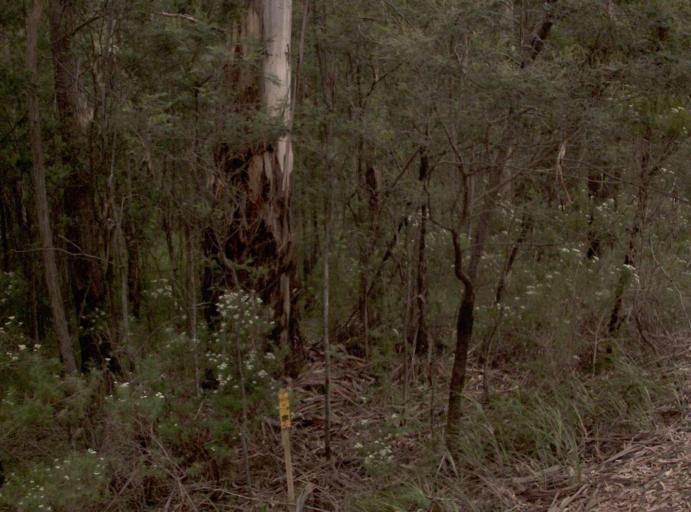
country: AU
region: Victoria
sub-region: East Gippsland
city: Bairnsdale
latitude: -37.7115
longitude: 147.5921
